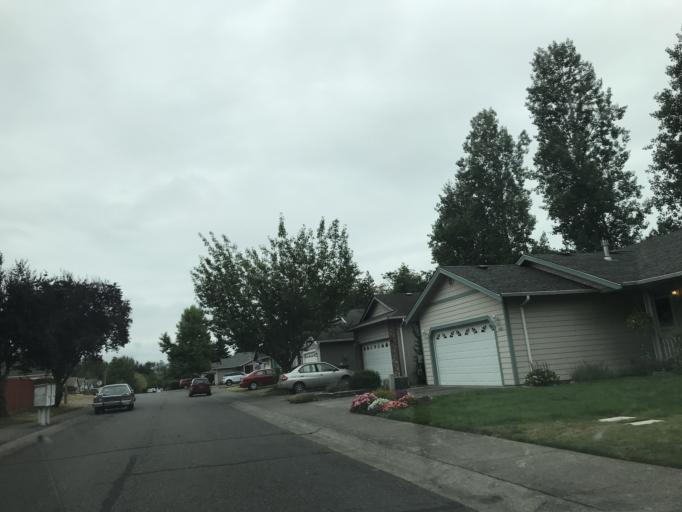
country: US
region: Washington
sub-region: Whatcom County
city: Bellingham
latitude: 48.7924
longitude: -122.4556
